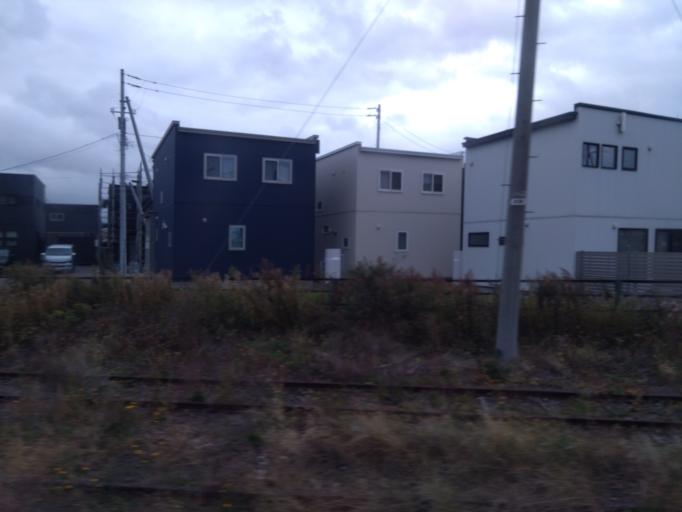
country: JP
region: Hokkaido
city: Hakodate
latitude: 41.8060
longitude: 140.7330
